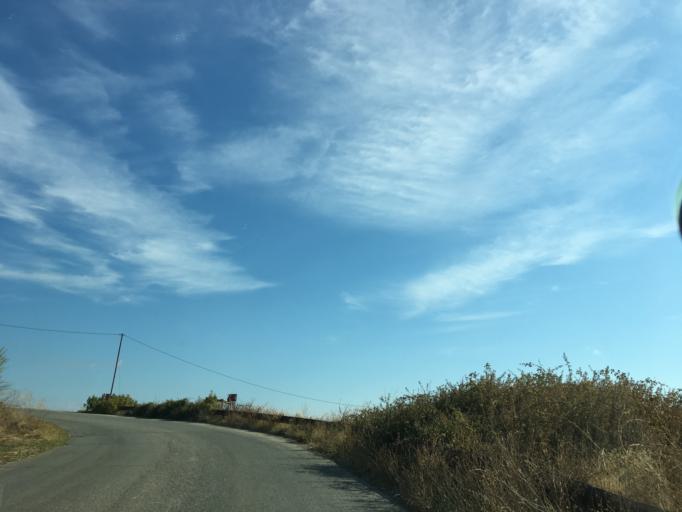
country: BG
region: Khaskovo
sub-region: Obshtina Ivaylovgrad
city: Ivaylovgrad
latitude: 41.5065
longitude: 26.1134
